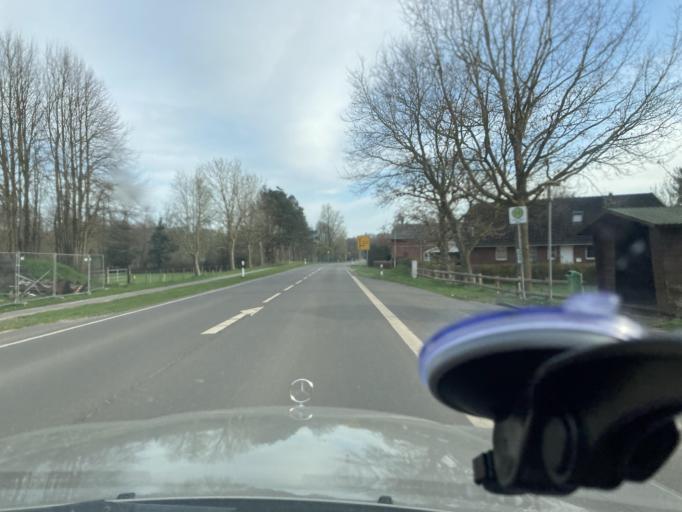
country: DE
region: Schleswig-Holstein
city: Stelle-Wittenwurth
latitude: 54.2735
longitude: 9.0472
